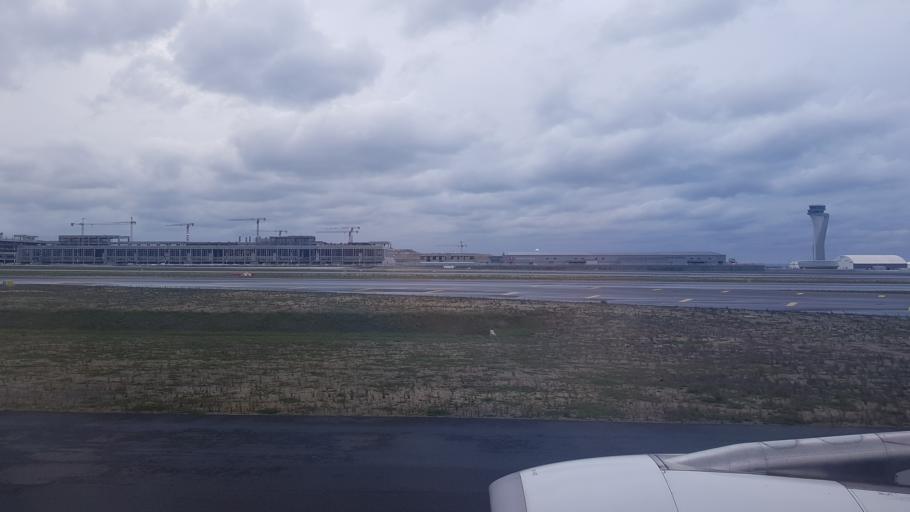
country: TR
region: Istanbul
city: Durusu
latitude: 41.2801
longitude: 28.7296
